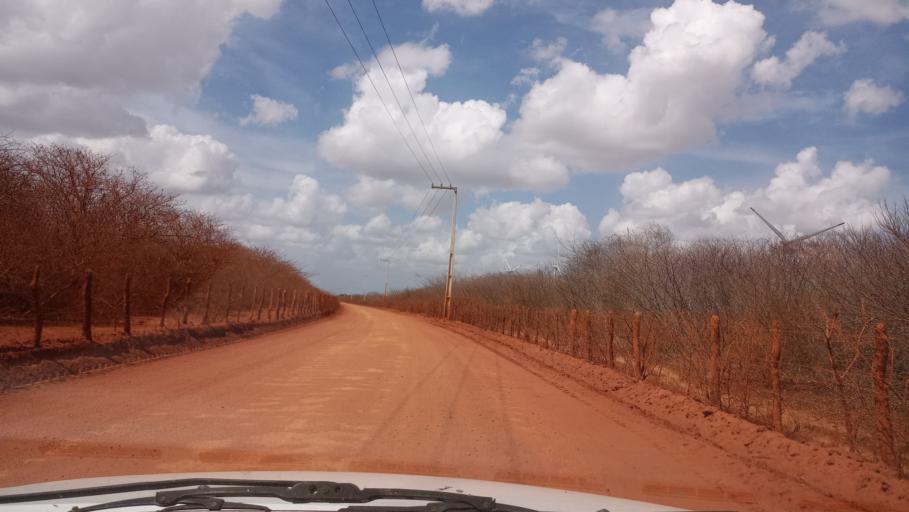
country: BR
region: Rio Grande do Norte
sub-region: Joao Camara
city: Joao Camara
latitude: -5.3628
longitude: -35.8358
